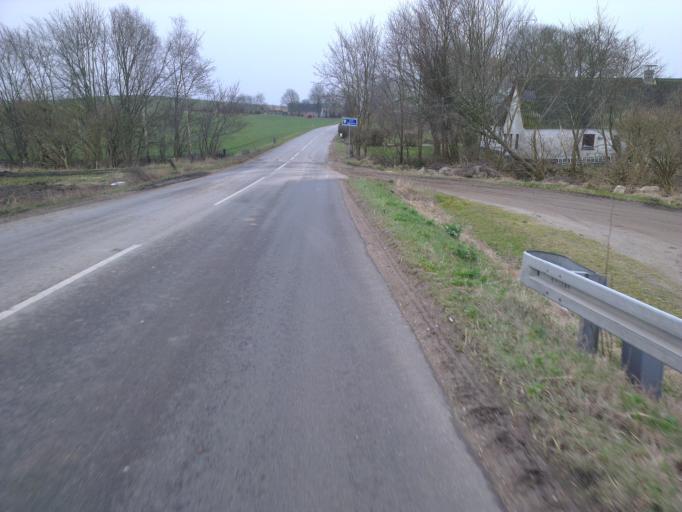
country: DK
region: Capital Region
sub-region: Frederikssund Kommune
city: Skibby
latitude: 55.7454
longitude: 11.9270
